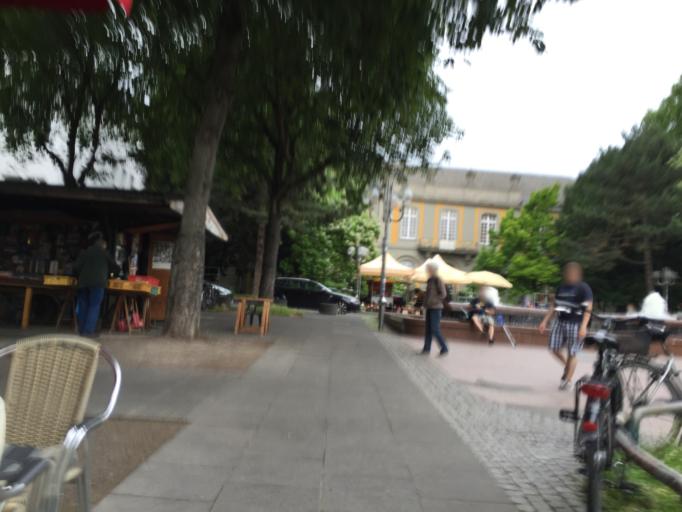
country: DE
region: North Rhine-Westphalia
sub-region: Regierungsbezirk Koln
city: Bonn
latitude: 50.7324
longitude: 7.1012
